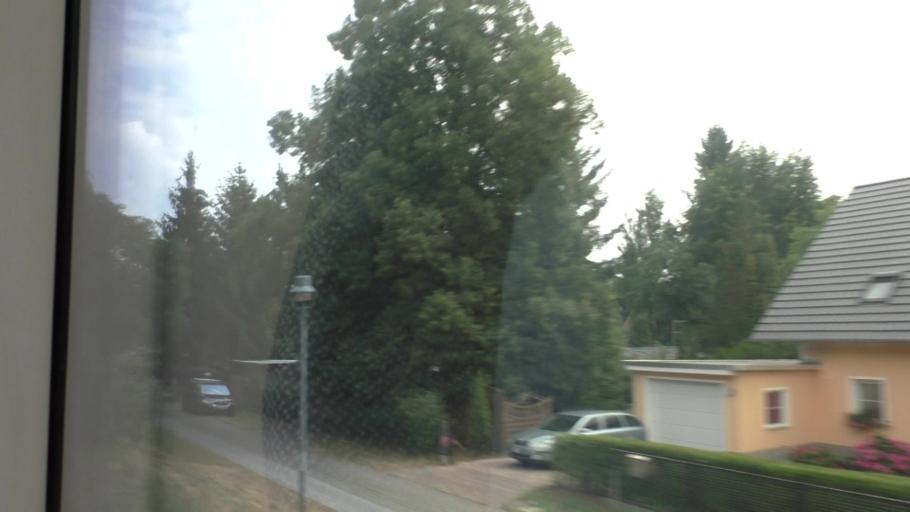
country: DE
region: Brandenburg
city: Konigs Wusterhausen
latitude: 52.3000
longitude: 13.6623
